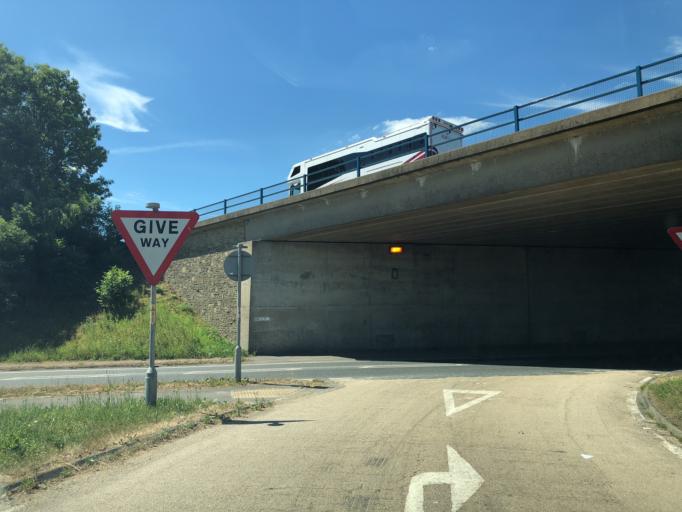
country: GB
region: England
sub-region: North Yorkshire
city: Thirsk
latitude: 54.2280
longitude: -1.3260
